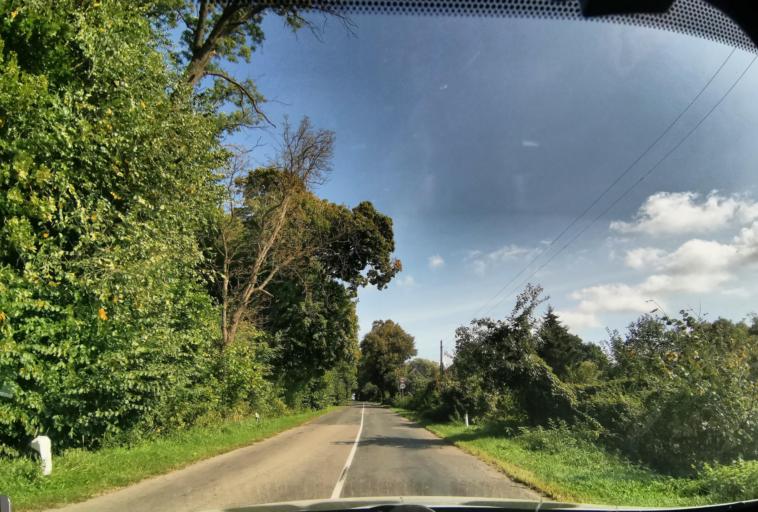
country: RU
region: Kaliningrad
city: Chernyakhovsk
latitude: 54.6487
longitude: 21.7734
